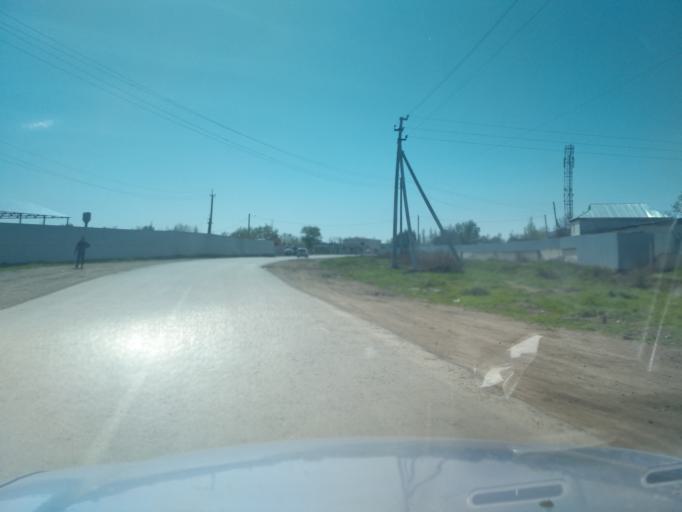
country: UZ
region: Sirdaryo
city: Guliston
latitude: 40.4962
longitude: 68.7999
